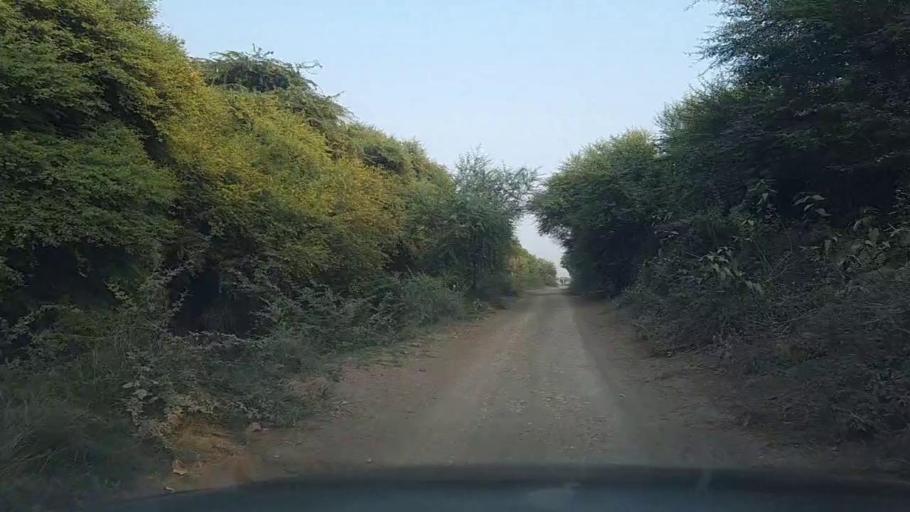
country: PK
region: Sindh
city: Mirpur Batoro
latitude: 24.5474
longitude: 68.3481
